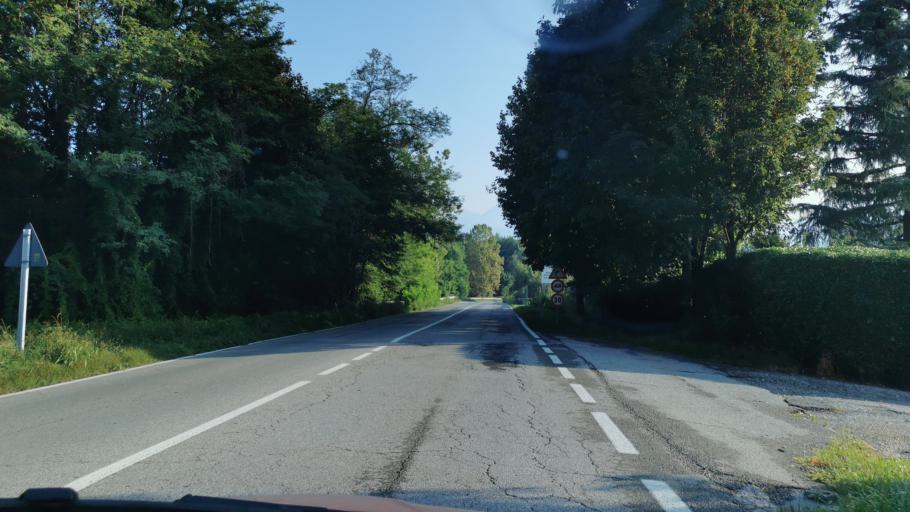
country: IT
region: Lombardy
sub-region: Provincia di Lecco
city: Sirtori
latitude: 45.7493
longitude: 9.3272
